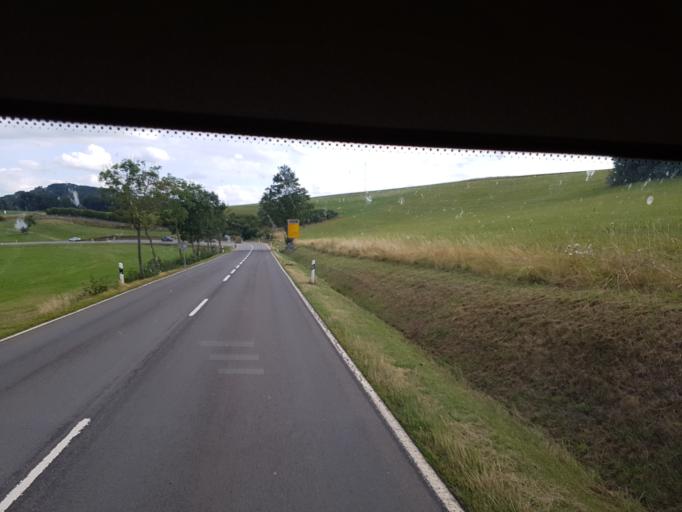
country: DE
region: Rheinland-Pfalz
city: Betteldorf
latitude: 50.2491
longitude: 6.7597
